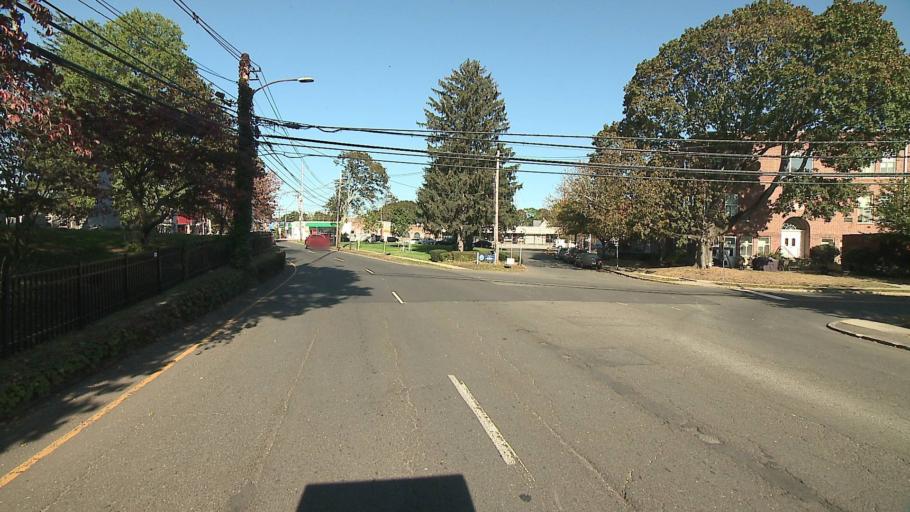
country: US
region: Connecticut
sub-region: Fairfield County
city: East Norwalk
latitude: 41.1025
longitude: -73.4028
